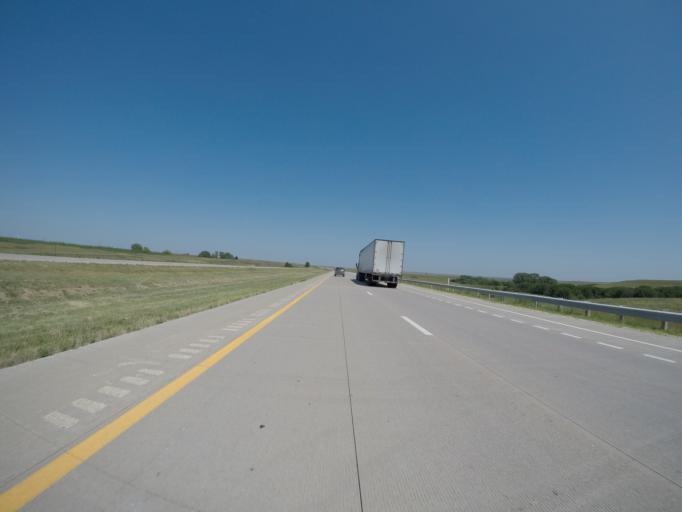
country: US
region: Kansas
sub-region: Ellsworth County
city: Ellsworth
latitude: 38.8485
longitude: -98.1753
